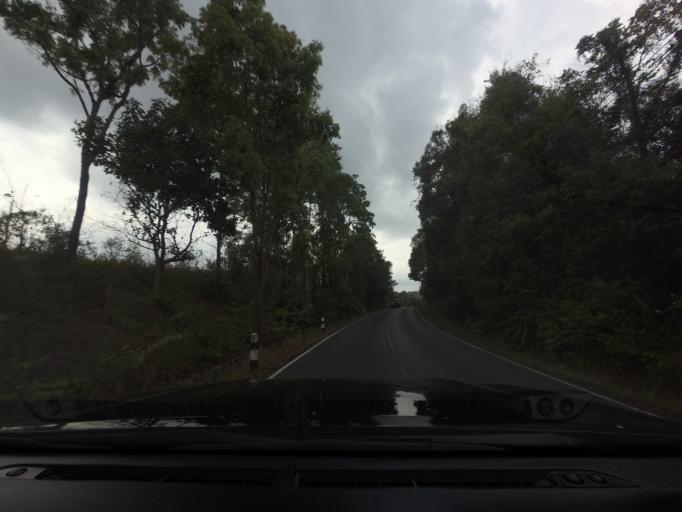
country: TH
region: Nakhon Nayok
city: Nakhon Nayok
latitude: 14.4237
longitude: 101.3703
